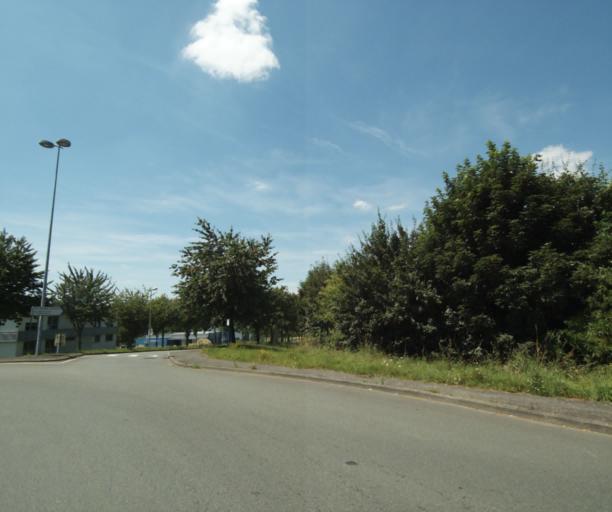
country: FR
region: Pays de la Loire
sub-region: Departement de la Mayenne
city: Laval
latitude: 48.0870
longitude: -0.7522
